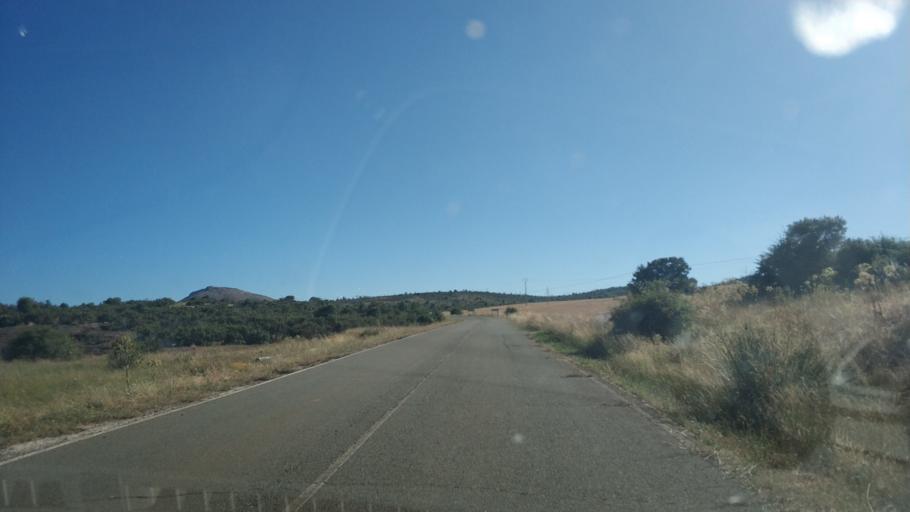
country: ES
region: Castille and Leon
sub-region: Provincia de Soria
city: Montejo de Tiermes
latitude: 41.3419
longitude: -3.1496
